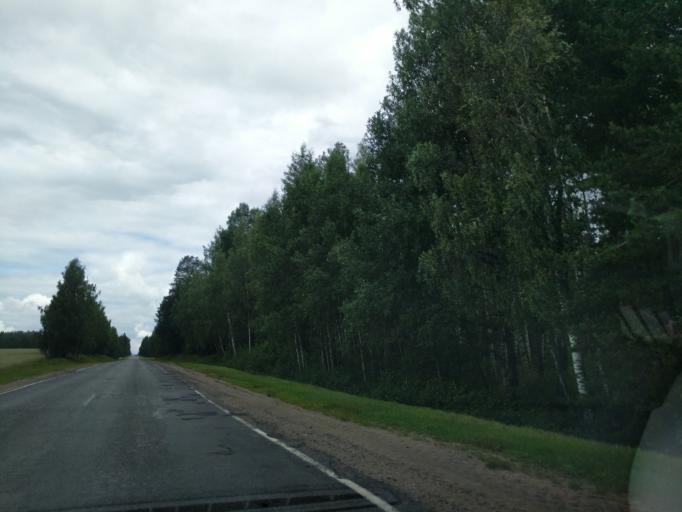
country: BY
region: Minsk
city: Kryvichy
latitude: 54.5777
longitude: 27.2006
